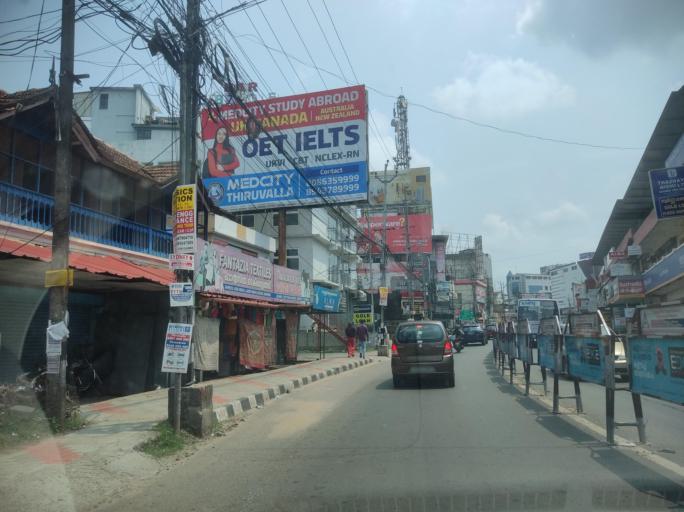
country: IN
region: Kerala
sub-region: Pattanamtitta
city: Tiruvalla
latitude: 9.3841
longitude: 76.5741
